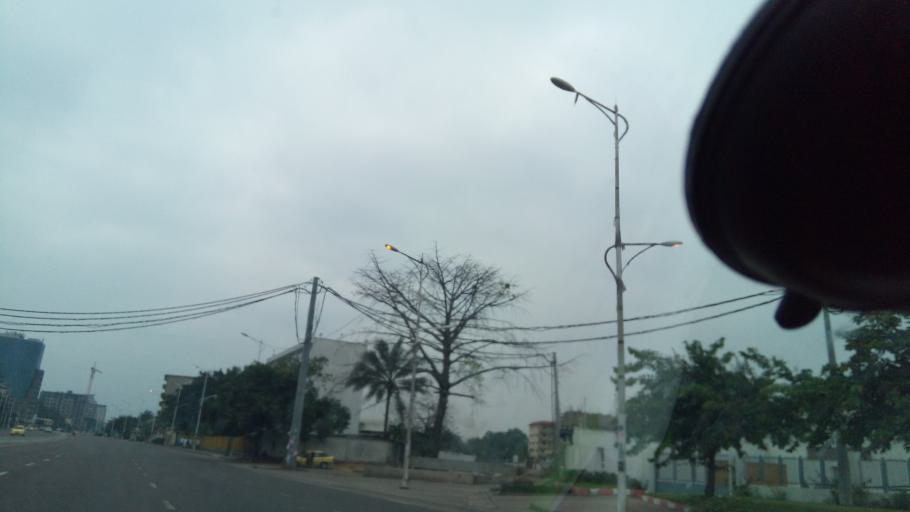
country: CD
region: Kinshasa
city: Kinshasa
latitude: -4.3201
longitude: 15.2755
